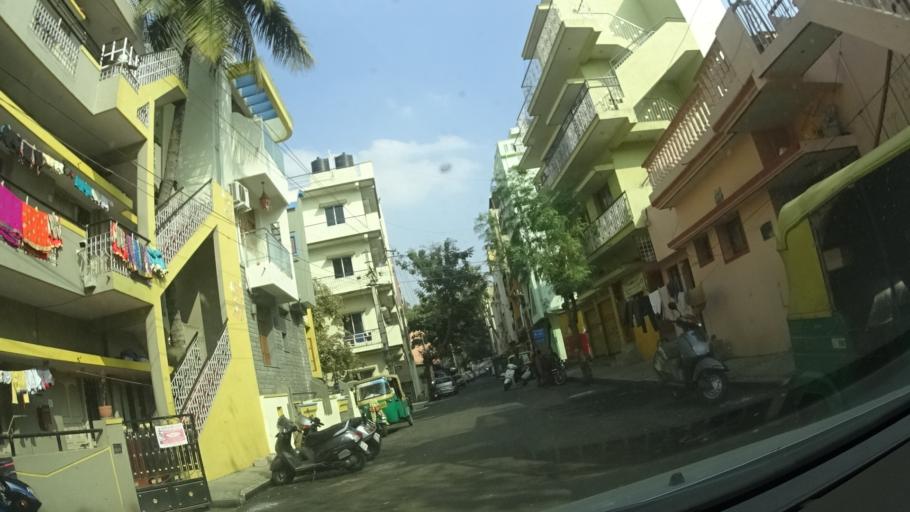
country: IN
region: Karnataka
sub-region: Bangalore Urban
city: Bangalore
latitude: 12.9474
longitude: 77.5610
